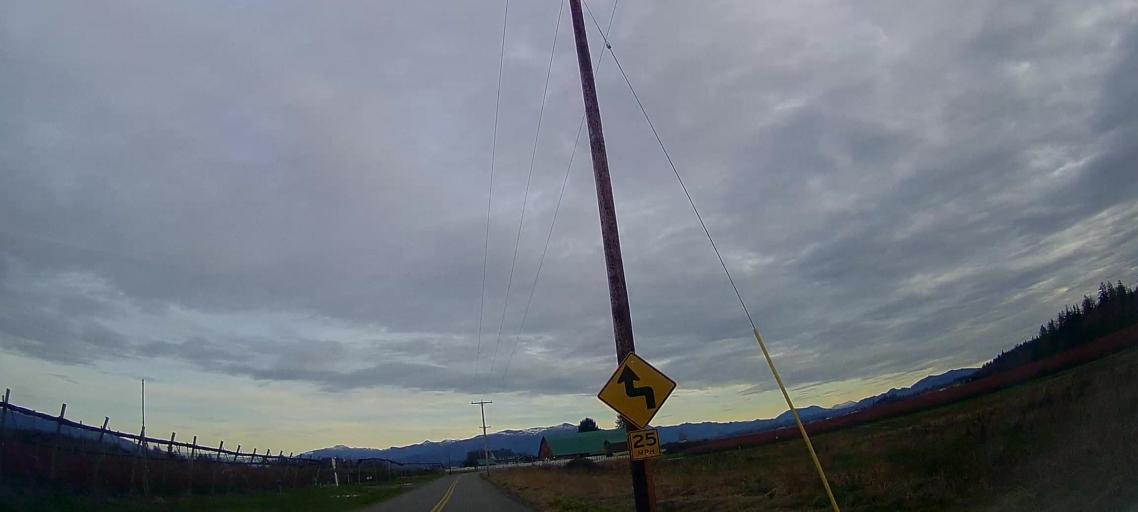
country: US
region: Washington
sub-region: Skagit County
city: Burlington
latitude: 48.5020
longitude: -122.4171
